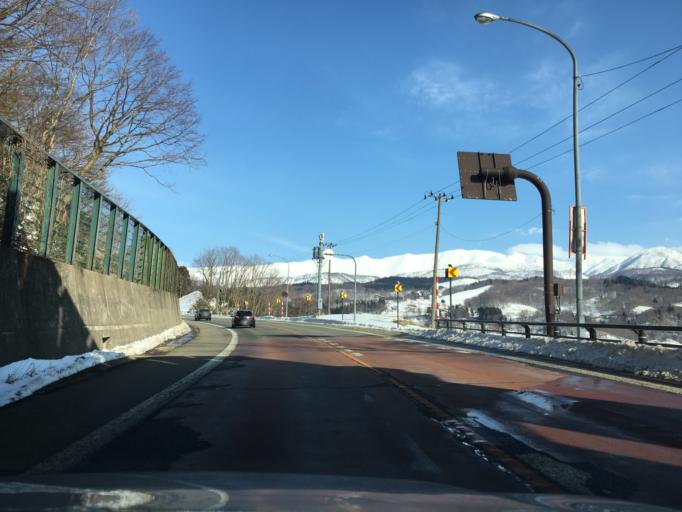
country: JP
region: Yamagata
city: Tsuruoka
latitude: 38.5753
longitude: 139.9243
